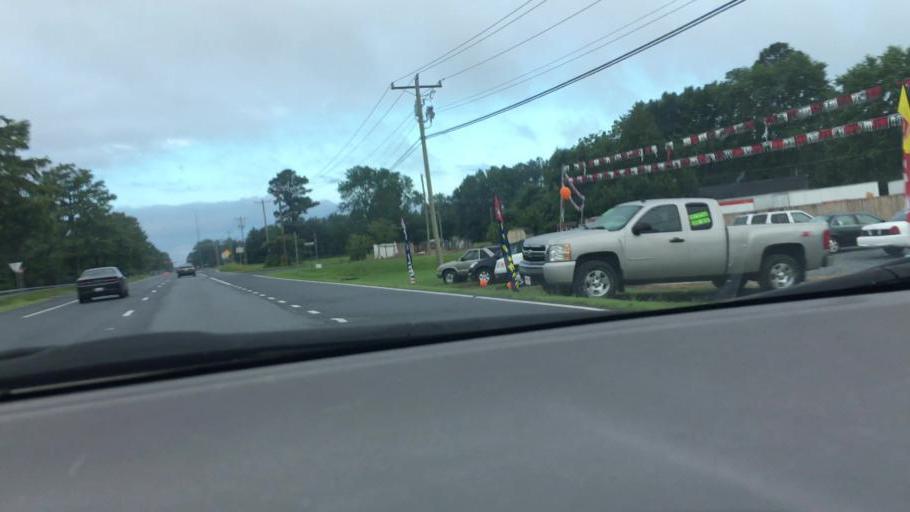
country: US
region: Maryland
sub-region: Wicomico County
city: Fruitland
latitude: 38.3190
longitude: -75.6222
